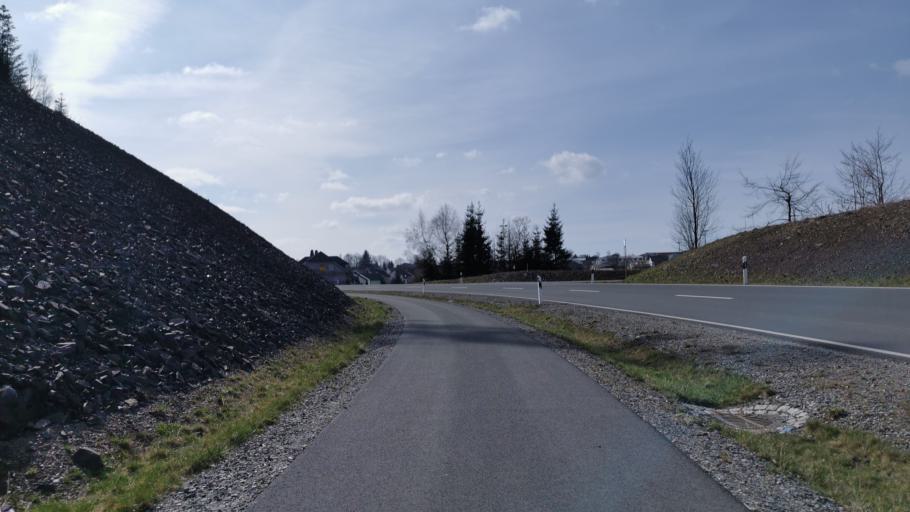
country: DE
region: Bavaria
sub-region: Upper Franconia
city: Teuschnitz
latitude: 50.4187
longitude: 11.3333
